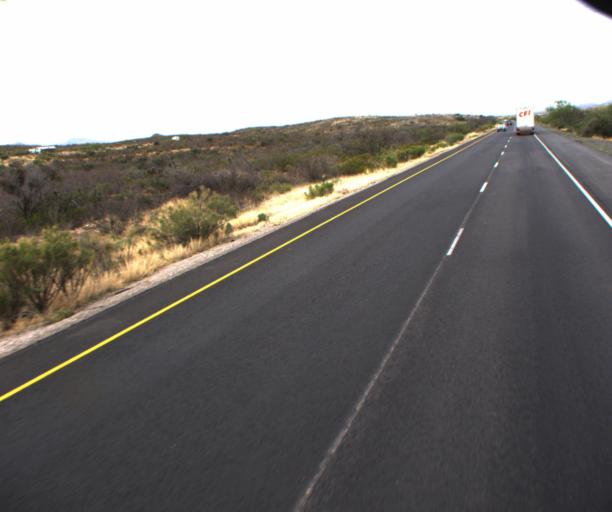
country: US
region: Arizona
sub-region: Cochise County
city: Mescal
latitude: 31.9697
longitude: -110.4727
